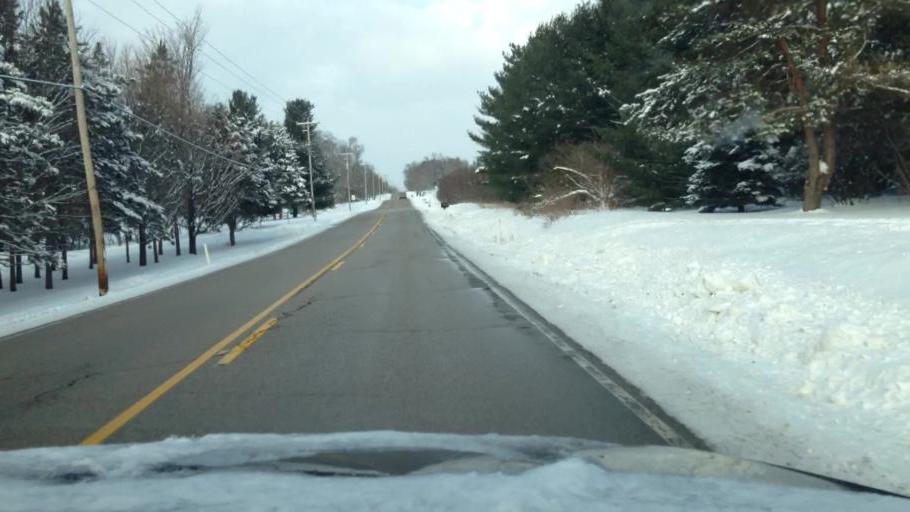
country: US
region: Wisconsin
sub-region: Waukesha County
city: Eagle
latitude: 42.8670
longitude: -88.4280
